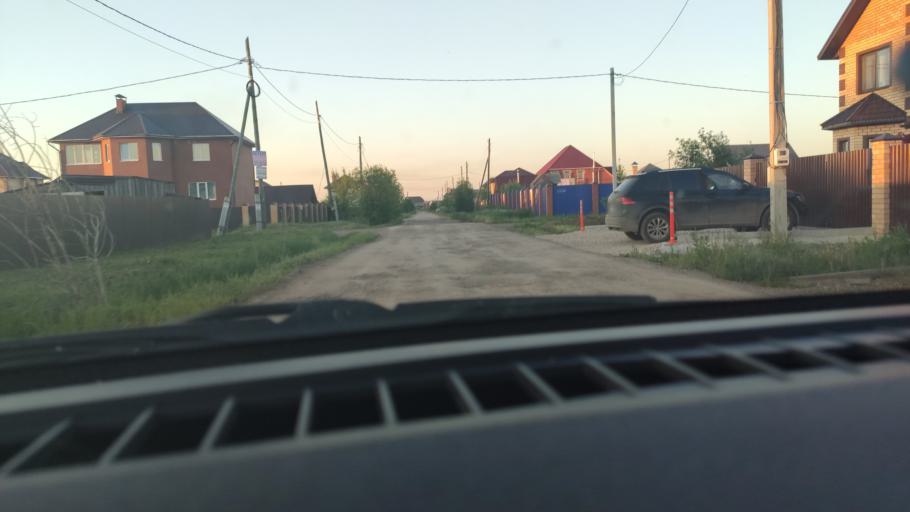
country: RU
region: Perm
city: Kultayevo
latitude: 57.8993
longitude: 55.9661
